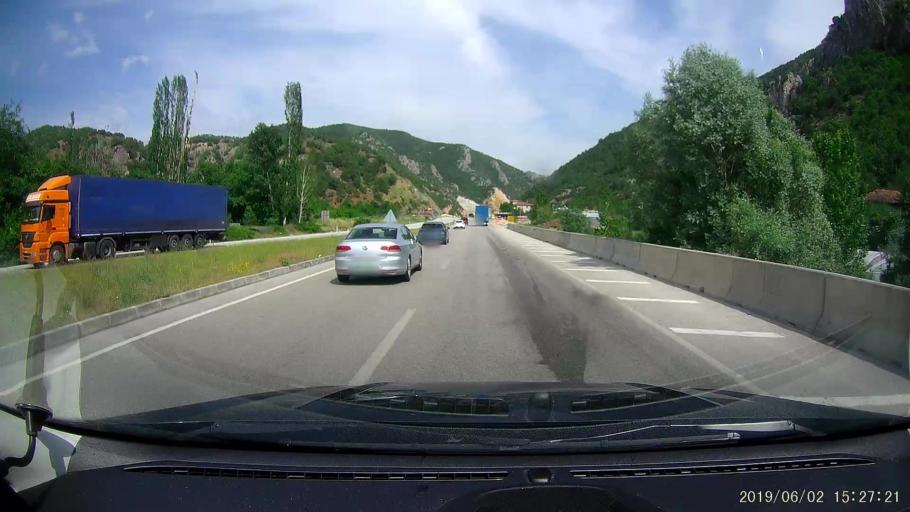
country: TR
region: Amasya
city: Saraycik
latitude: 40.9834
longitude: 35.0560
